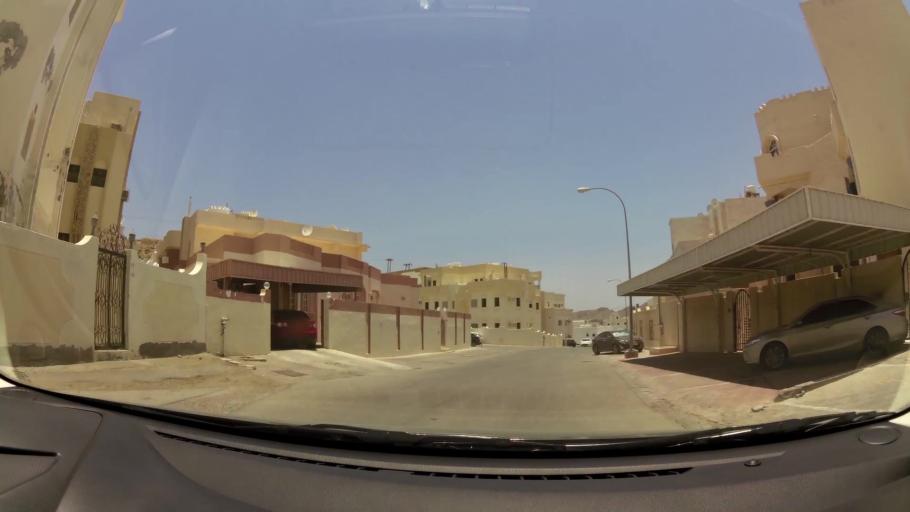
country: OM
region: Muhafazat Masqat
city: Muscat
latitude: 23.6143
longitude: 58.5338
